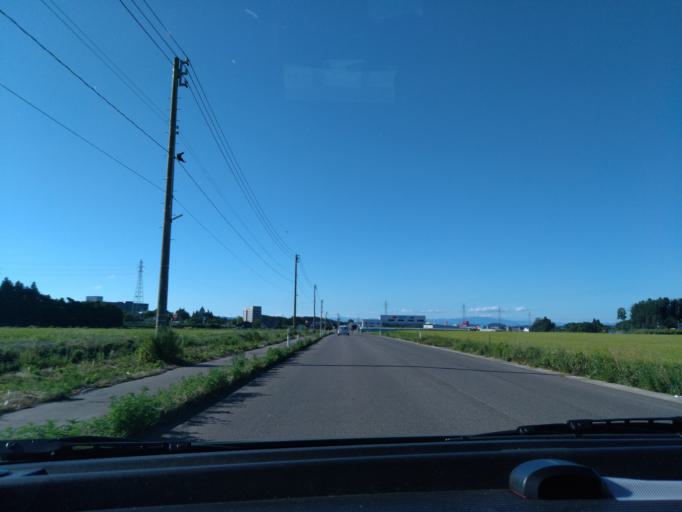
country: JP
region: Akita
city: Yokotemachi
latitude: 39.2858
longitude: 140.5555
